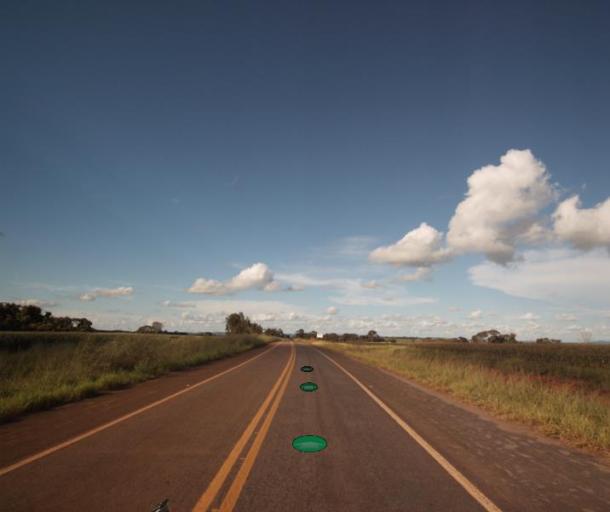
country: BR
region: Goias
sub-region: Itaberai
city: Itaberai
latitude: -15.9841
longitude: -49.6927
